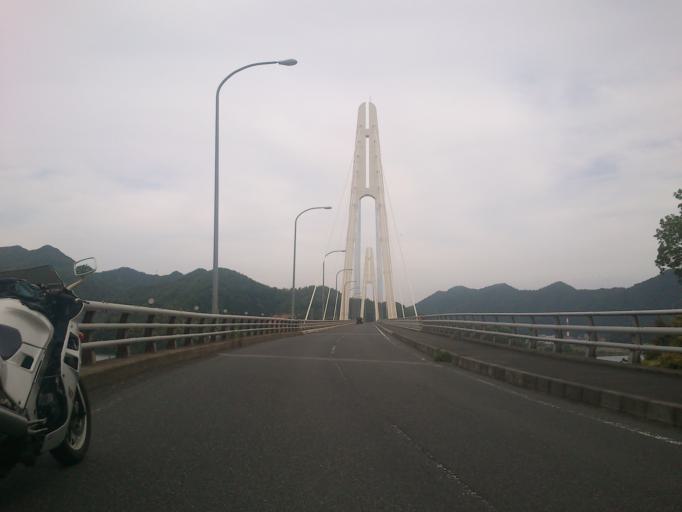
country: JP
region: Kyoto
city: Maizuru
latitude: 35.5111
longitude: 135.3840
